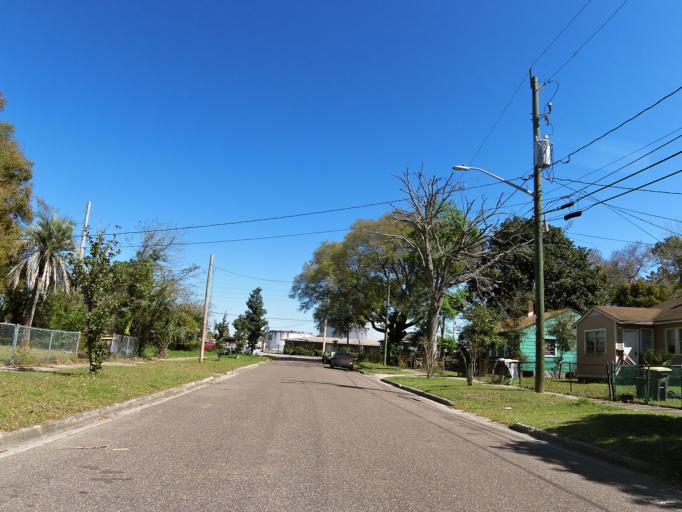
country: US
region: Florida
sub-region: Duval County
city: Jacksonville
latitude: 30.3612
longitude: -81.6282
